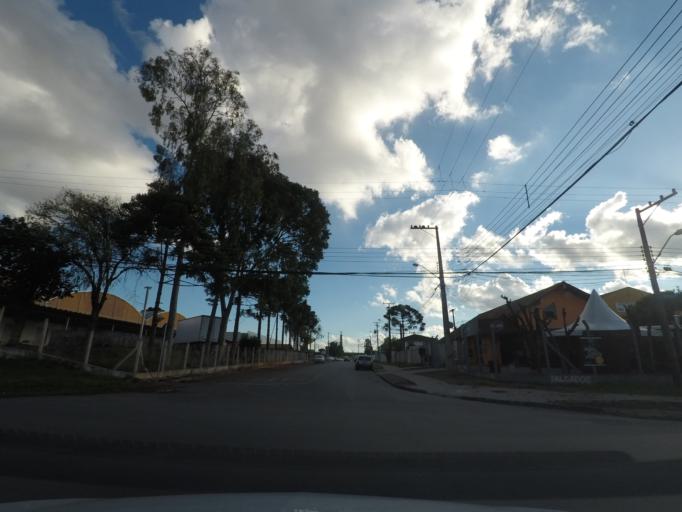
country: BR
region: Parana
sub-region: Curitiba
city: Curitiba
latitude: -25.4828
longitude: -49.2619
